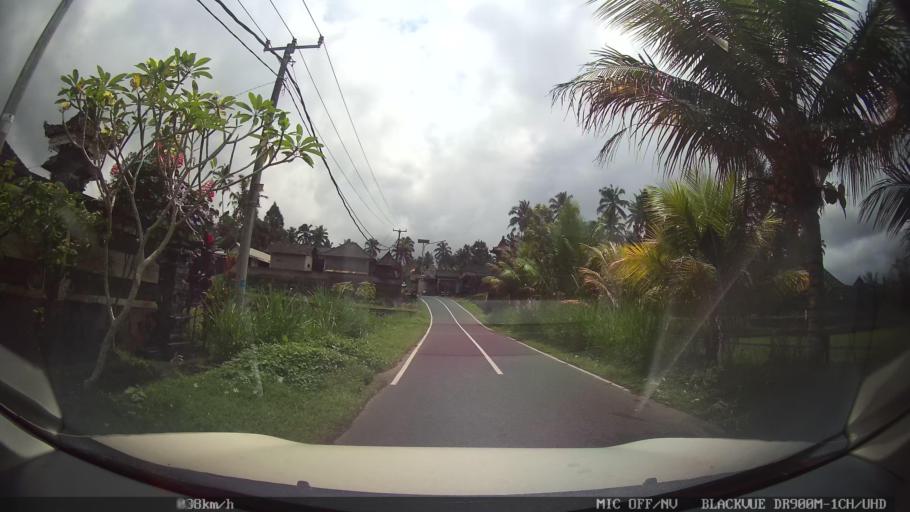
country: ID
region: Bali
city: Banjar Geriana Kangin
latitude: -8.4183
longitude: 115.4368
